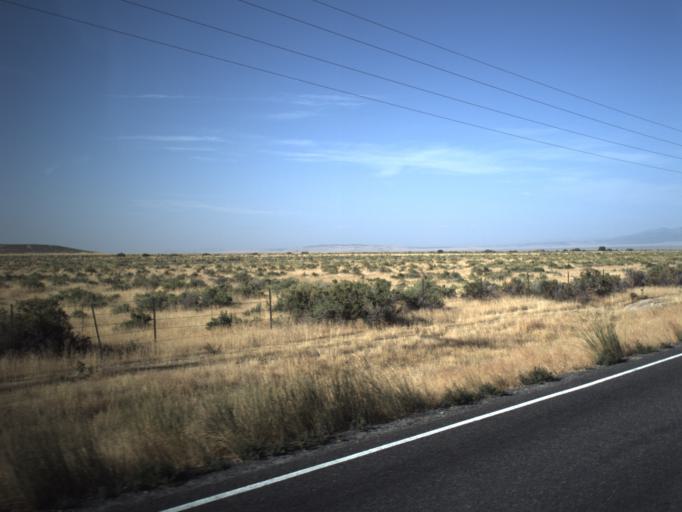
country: US
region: Idaho
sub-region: Oneida County
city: Malad City
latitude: 41.9667
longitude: -112.7868
